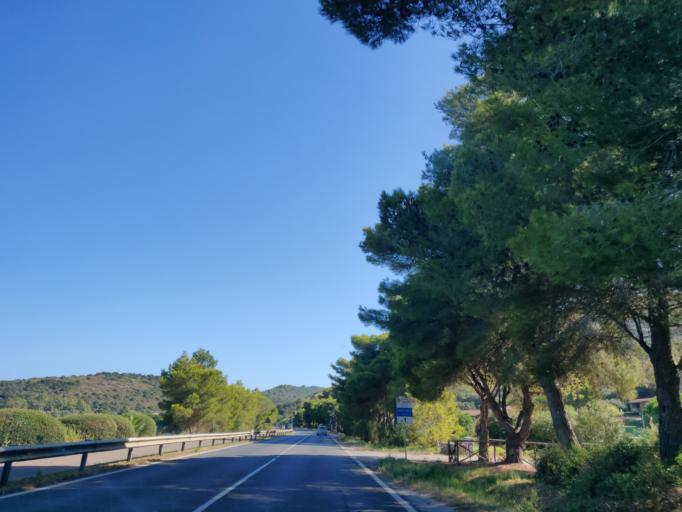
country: IT
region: Tuscany
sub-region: Provincia di Grosseto
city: Porto Ercole
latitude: 42.4208
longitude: 11.2028
